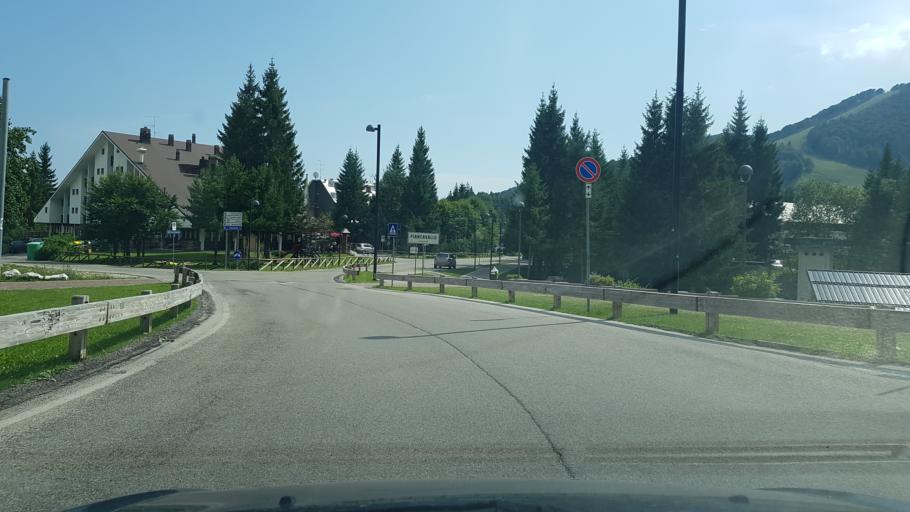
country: IT
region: Friuli Venezia Giulia
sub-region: Provincia di Pordenone
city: Budoia
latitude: 46.1098
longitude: 12.5168
